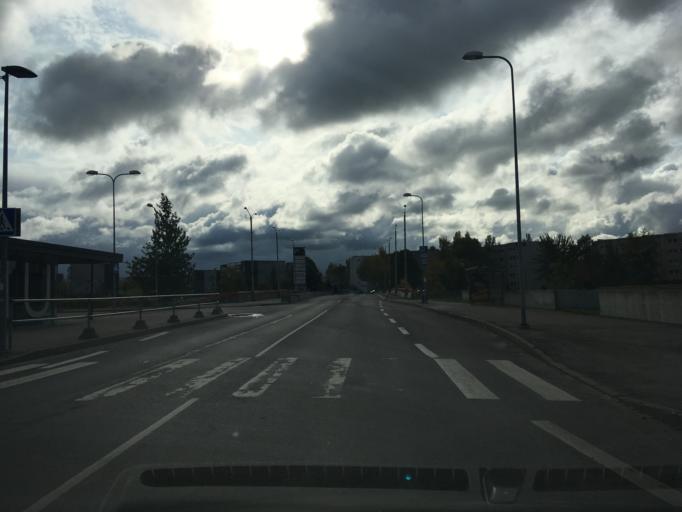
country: EE
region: Harju
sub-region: Tallinna linn
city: Tallinn
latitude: 59.4359
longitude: 24.7986
